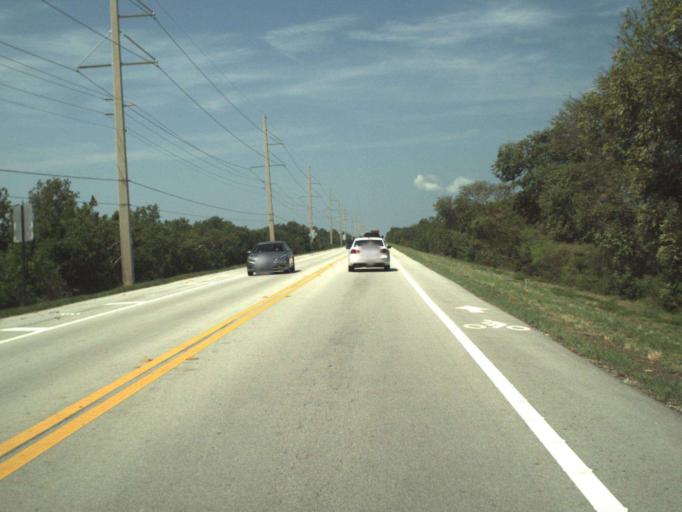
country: US
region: Florida
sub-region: Monroe County
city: Marathon
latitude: 24.7887
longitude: -80.8910
